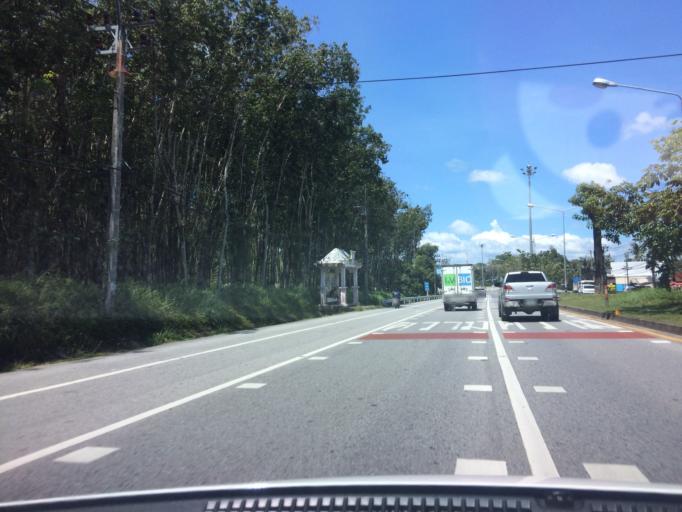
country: TH
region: Phuket
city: Thalang
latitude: 8.1528
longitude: 98.3386
